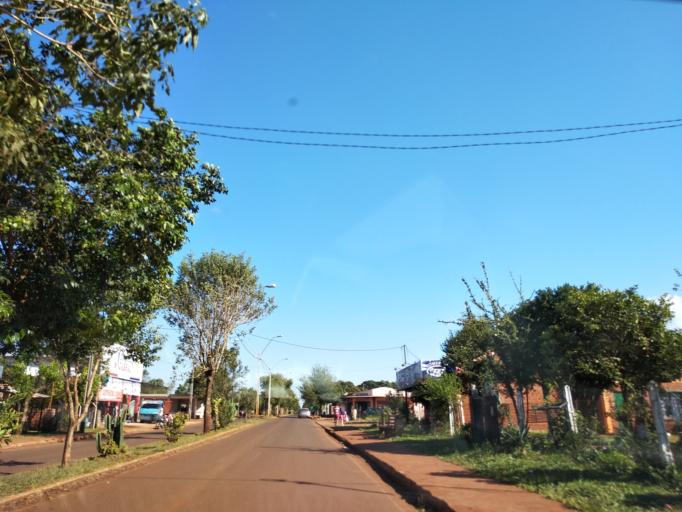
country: PY
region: Itapua
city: Hohenau
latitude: -27.0584
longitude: -55.7386
